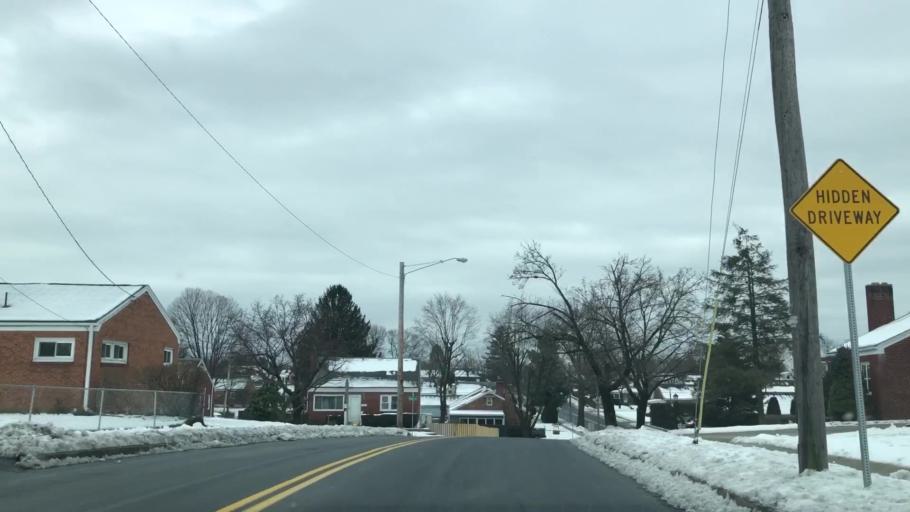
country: US
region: Pennsylvania
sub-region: Dauphin County
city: Colonial Park
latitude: 40.2973
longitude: -76.8063
